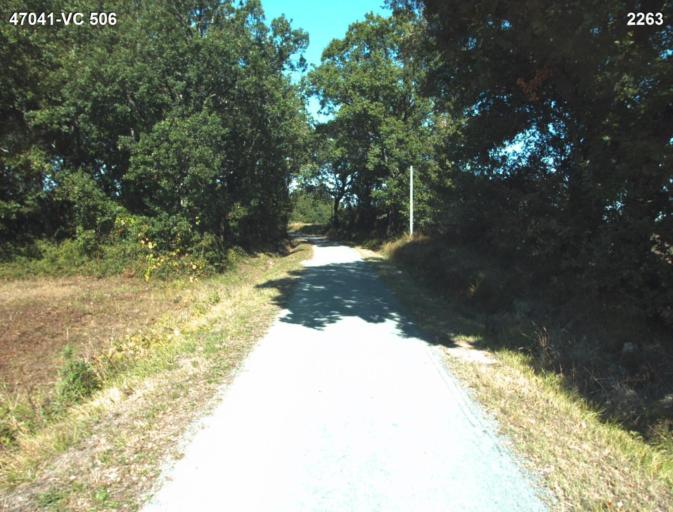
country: FR
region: Aquitaine
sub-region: Departement du Lot-et-Garonne
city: Port-Sainte-Marie
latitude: 44.1967
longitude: 0.3856
